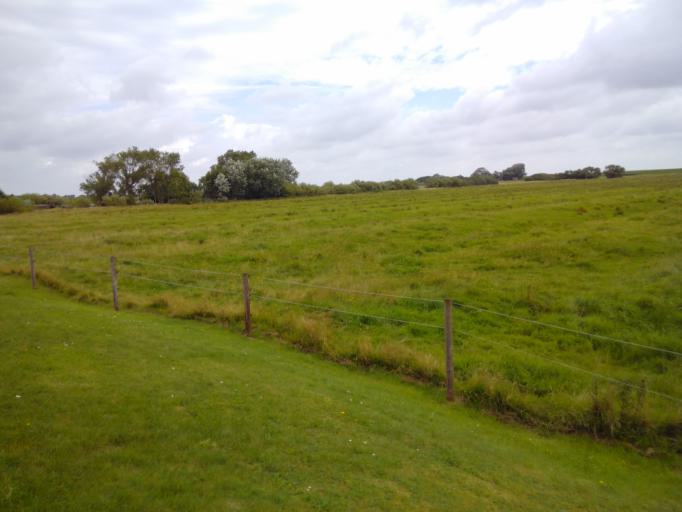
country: DE
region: Lower Saxony
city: Nordholz
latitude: 53.9148
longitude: 8.4973
